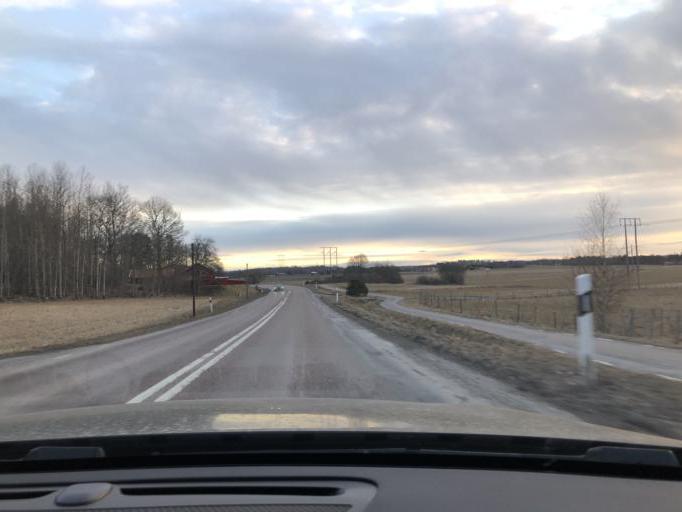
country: SE
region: Uppsala
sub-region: Uppsala Kommun
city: Gamla Uppsala
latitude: 59.9334
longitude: 17.6435
